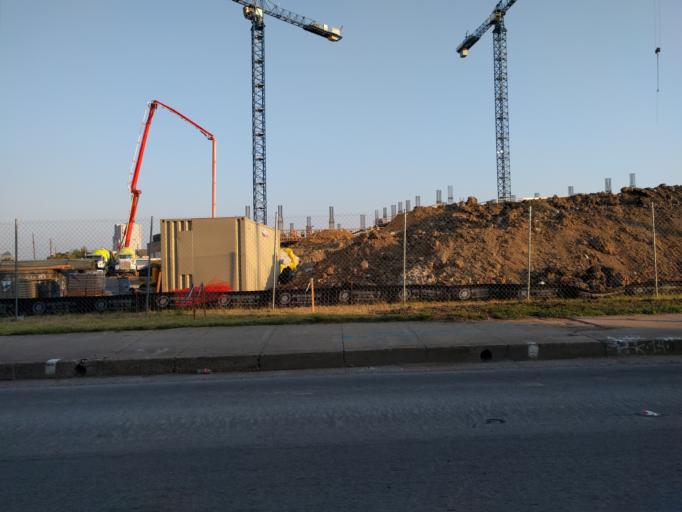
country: US
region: Texas
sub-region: Dallas County
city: Dallas
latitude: 32.7837
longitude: -96.7883
